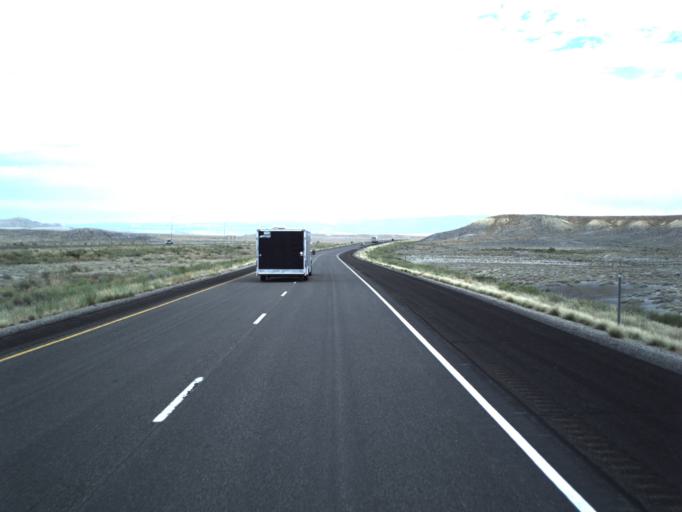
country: US
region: Utah
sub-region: Grand County
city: Moab
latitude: 38.9500
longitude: -109.6846
